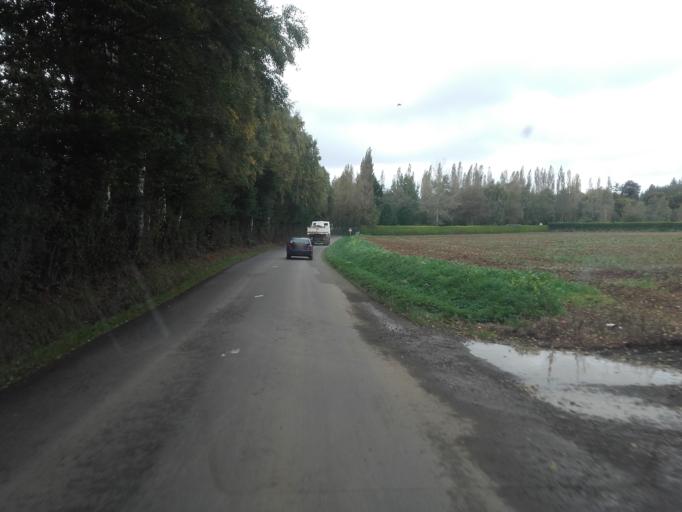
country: FR
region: Brittany
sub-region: Departement des Cotes-d'Armor
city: Plelo
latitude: 48.5797
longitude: -2.9480
